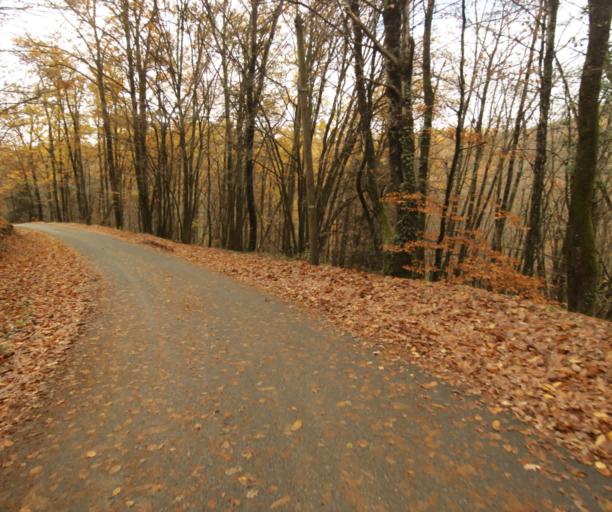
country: FR
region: Limousin
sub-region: Departement de la Correze
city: Sainte-Fereole
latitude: 45.2131
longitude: 1.6321
